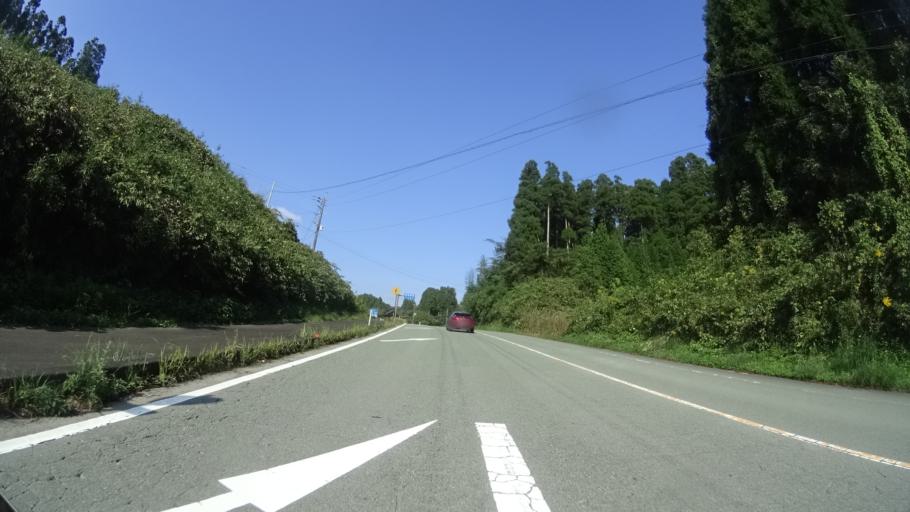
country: JP
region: Oita
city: Tsukawaki
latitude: 33.1517
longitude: 131.1093
